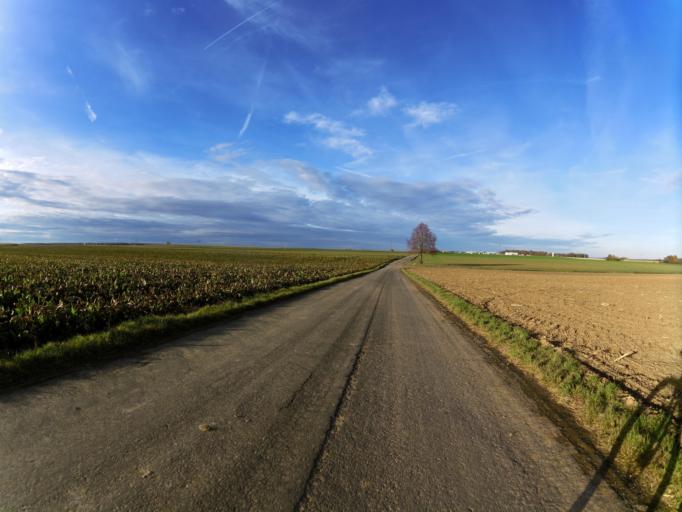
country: DE
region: Bavaria
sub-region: Regierungsbezirk Unterfranken
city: Giebelstadt
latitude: 49.6717
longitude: 9.9399
